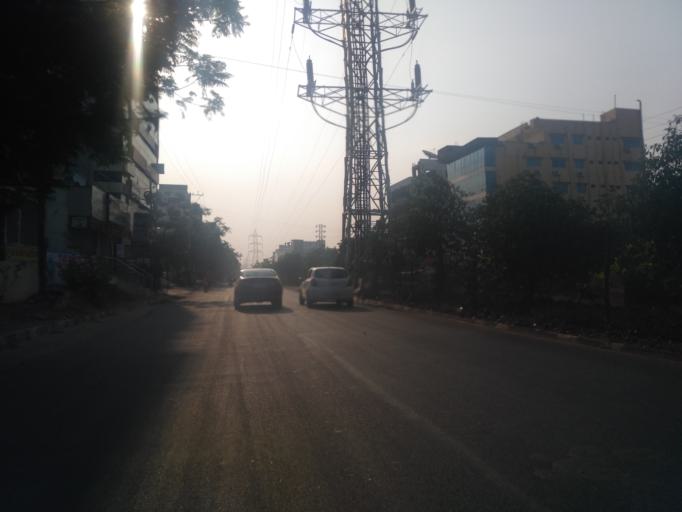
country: IN
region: Telangana
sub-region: Rangareddi
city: Kukatpalli
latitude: 17.4523
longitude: 78.3884
